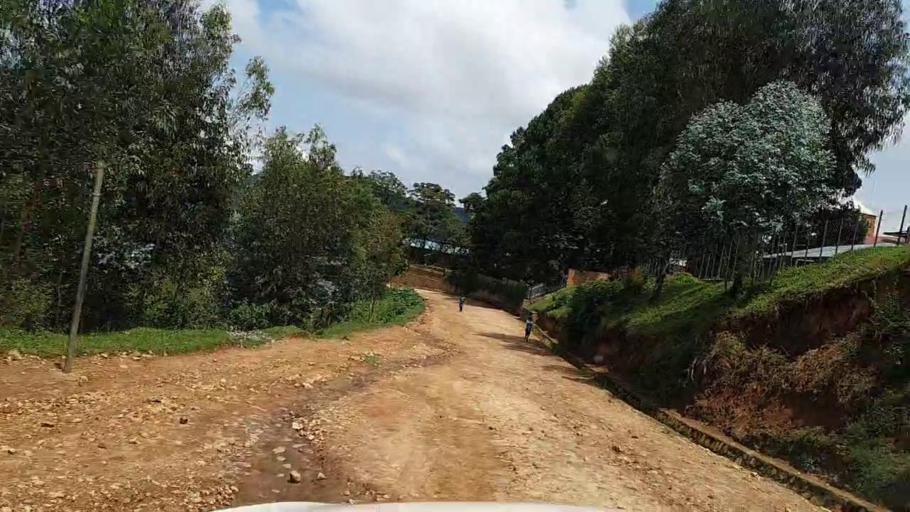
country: RW
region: Southern Province
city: Gikongoro
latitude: -2.3350
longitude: 29.5220
